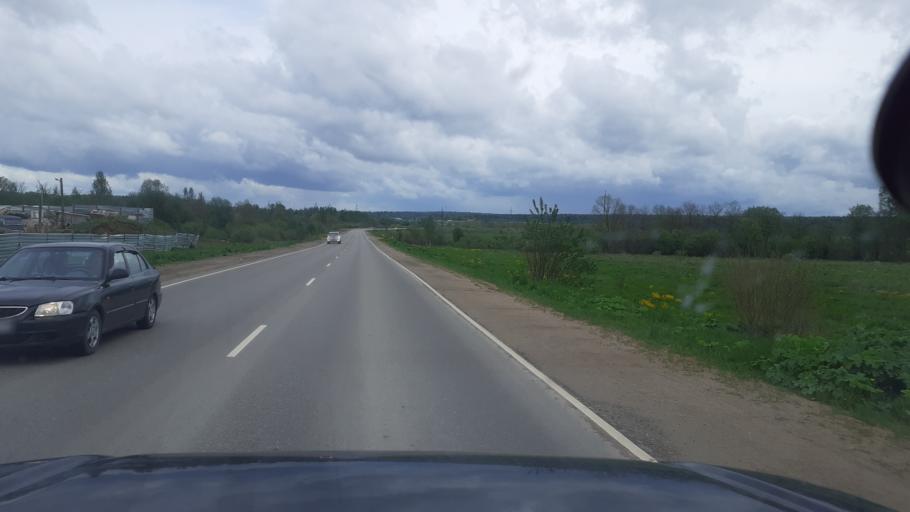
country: RU
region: Moskovskaya
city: Sychevo
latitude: 55.9827
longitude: 36.2181
